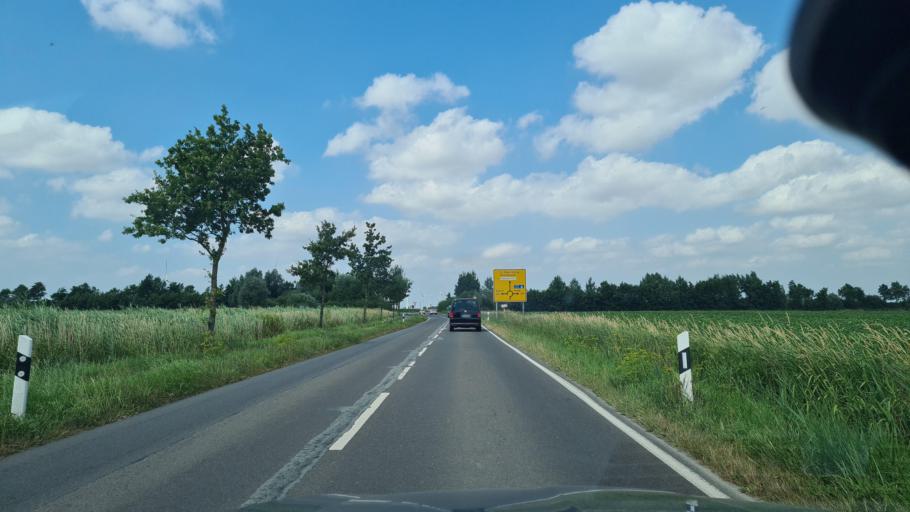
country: DE
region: Schleswig-Holstein
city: Wohrden
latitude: 54.1701
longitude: 8.9881
